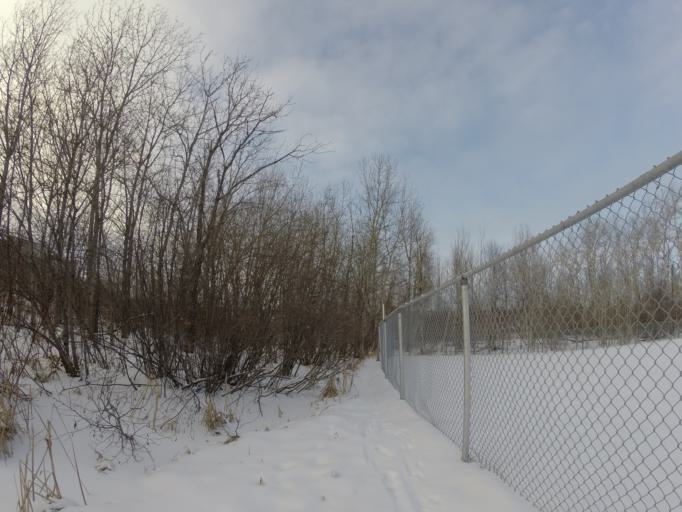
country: CA
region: Ontario
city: Greater Sudbury
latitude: 46.4695
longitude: -81.0023
